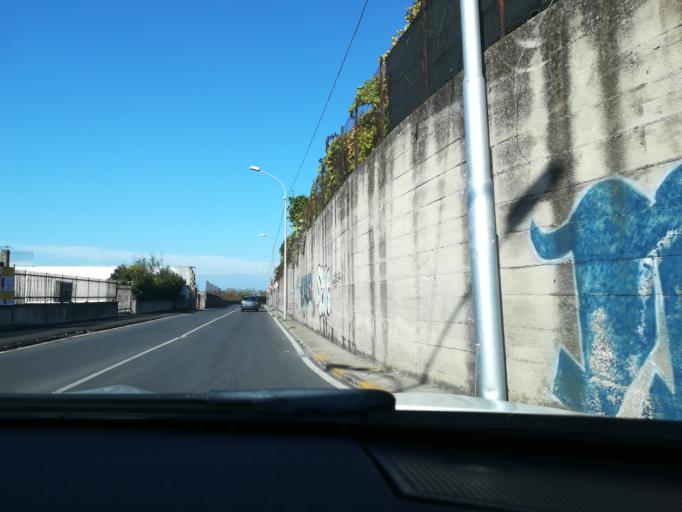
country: IT
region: Campania
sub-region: Provincia di Napoli
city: Sant'Anastasia
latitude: 40.8701
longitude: 14.3947
